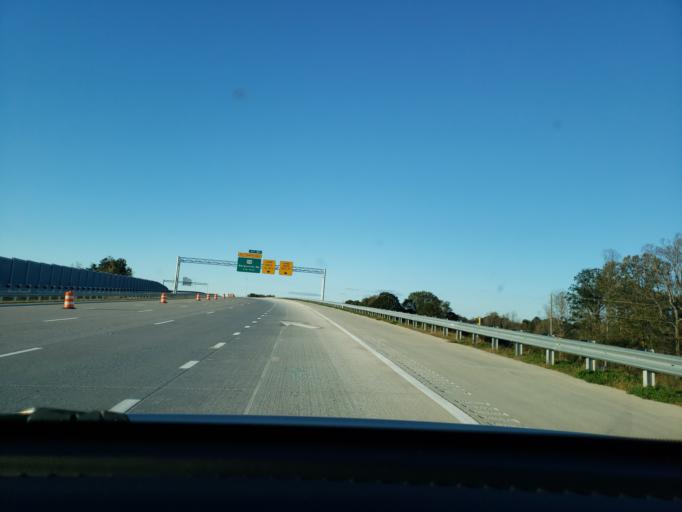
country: US
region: North Carolina
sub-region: Forsyth County
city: Kernersville
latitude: 36.1248
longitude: -80.1290
